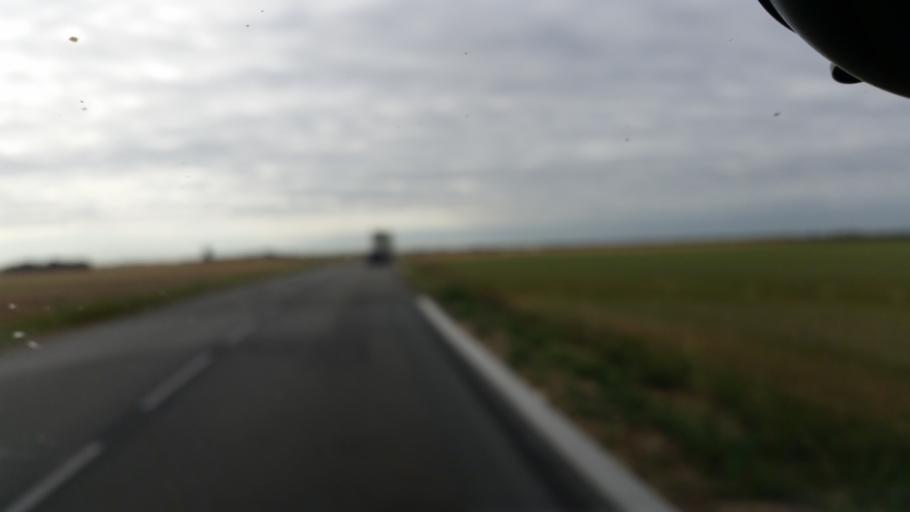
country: FR
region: Poitou-Charentes
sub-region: Departement de la Charente-Maritime
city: Marans
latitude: 46.2961
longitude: -0.9707
